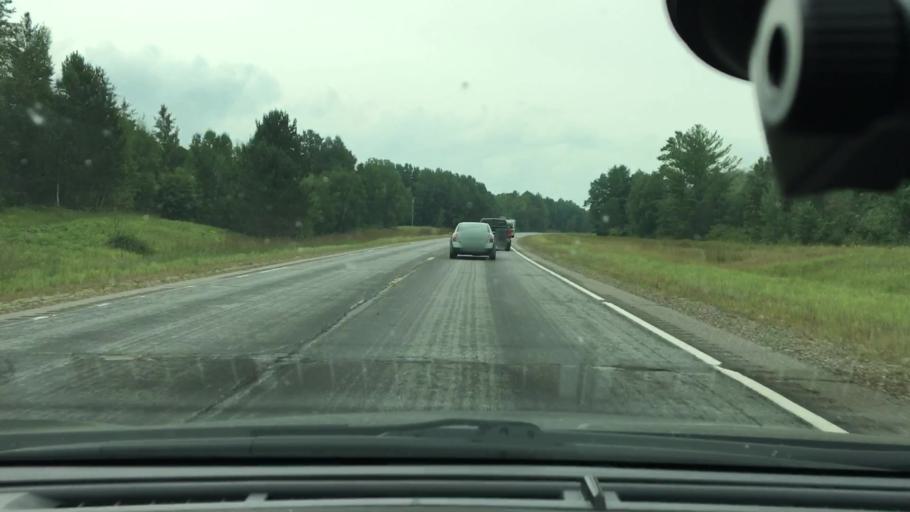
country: US
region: Minnesota
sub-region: Crow Wing County
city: Cross Lake
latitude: 46.6720
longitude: -93.9518
